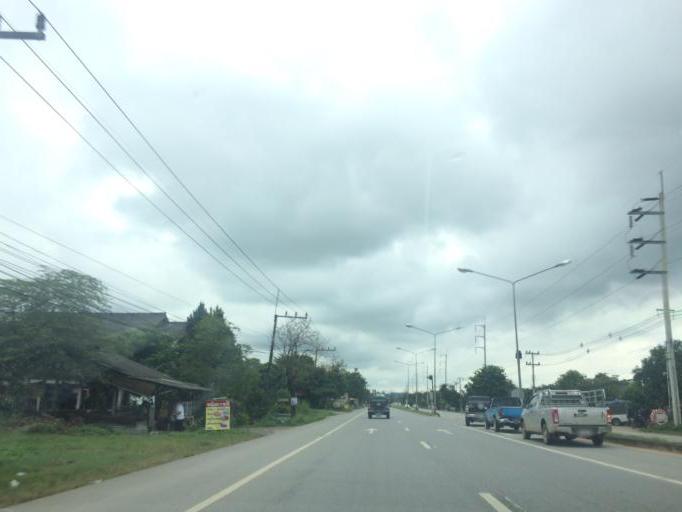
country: TH
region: Chiang Rai
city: Mae Chan
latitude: 20.0762
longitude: 99.8755
